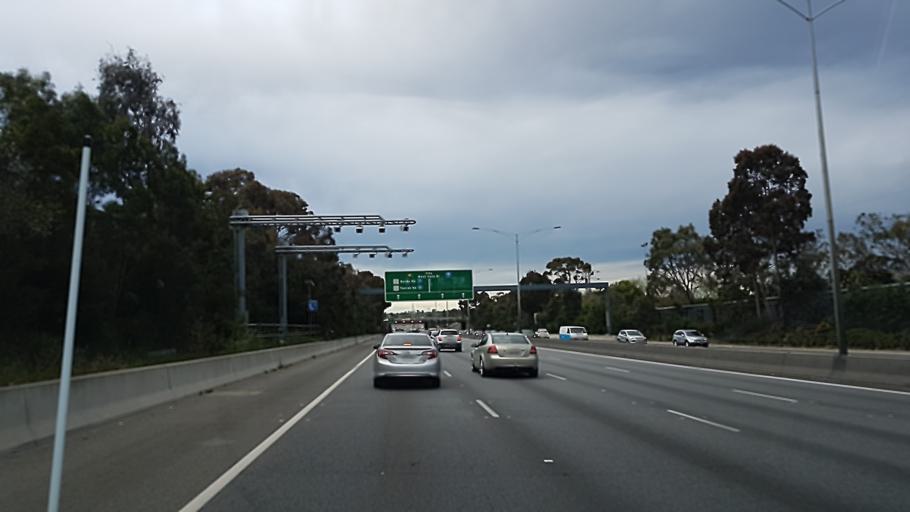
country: AU
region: Victoria
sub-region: Stonnington
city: Glen Iris
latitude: -37.8630
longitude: 145.0600
